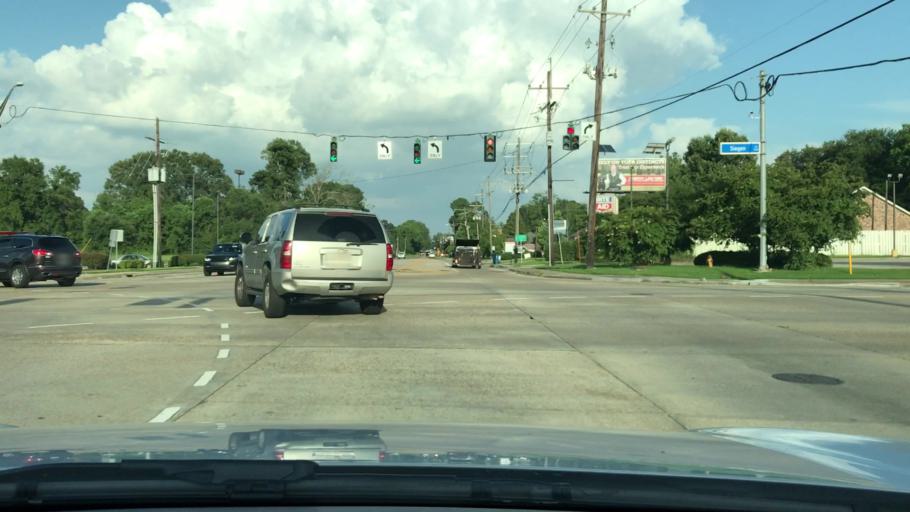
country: US
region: Louisiana
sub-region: East Baton Rouge Parish
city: Village Saint George
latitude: 30.3683
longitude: -91.0747
